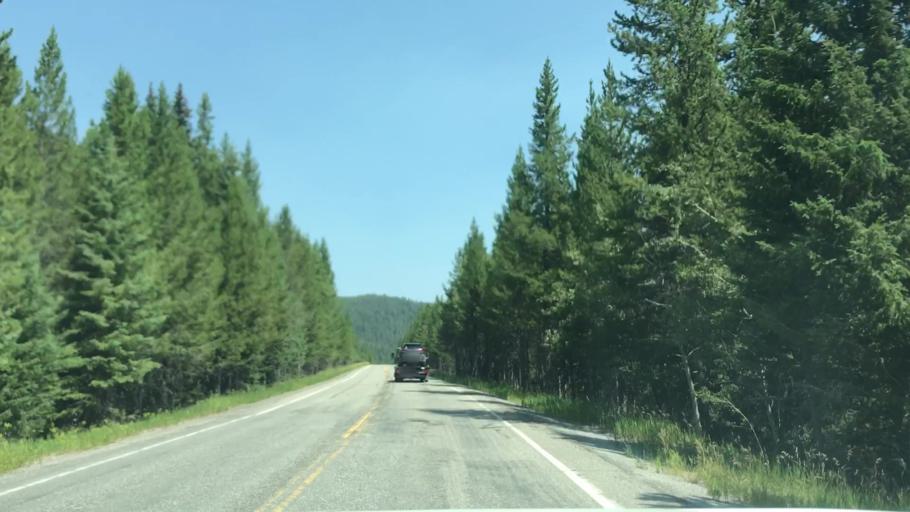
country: US
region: Montana
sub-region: Gallatin County
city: West Yellowstone
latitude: 44.8115
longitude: -111.0942
